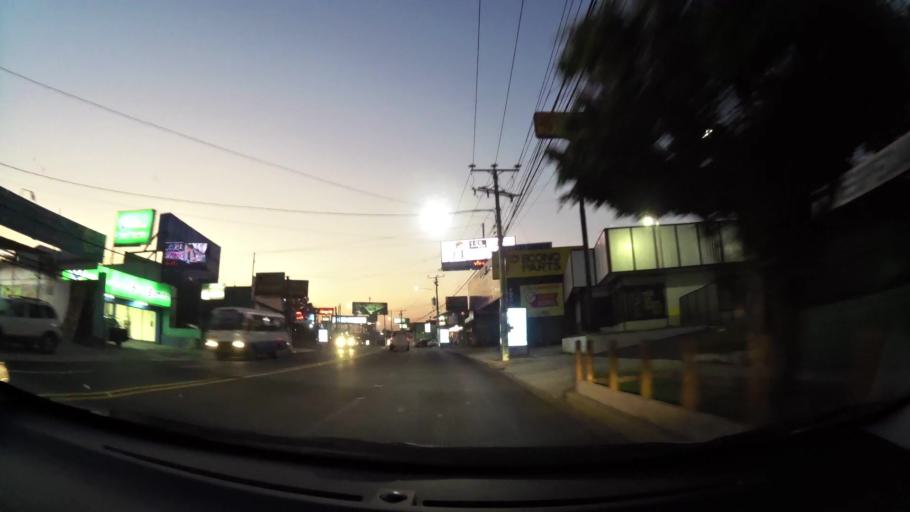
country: SV
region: La Libertad
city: Santa Tecla
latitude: 13.6788
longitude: -89.2689
